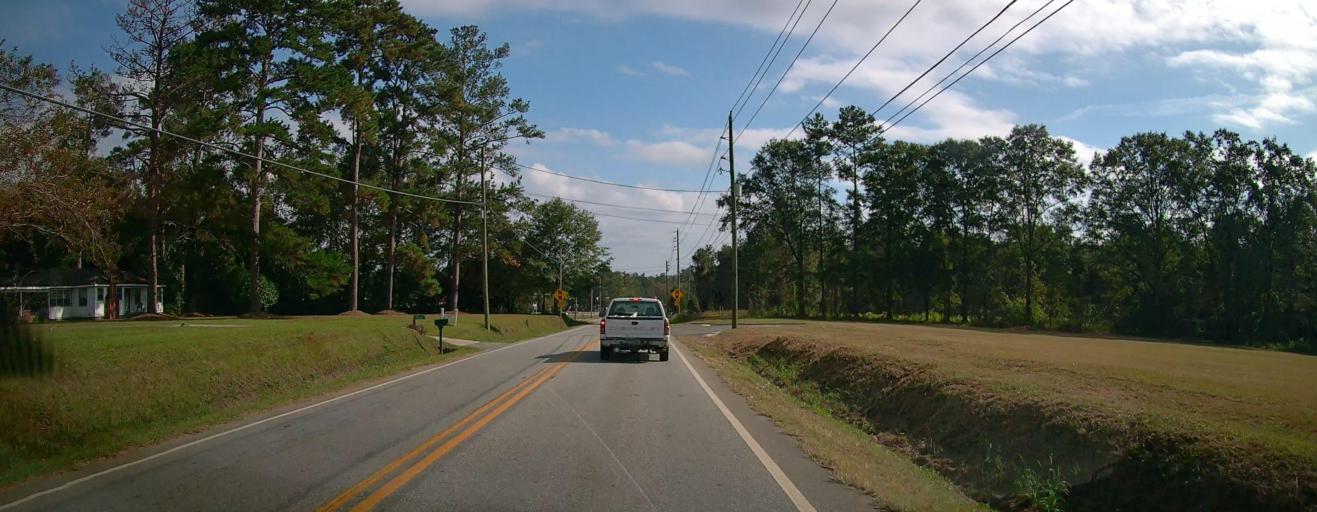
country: US
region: Georgia
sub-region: Thomas County
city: Thomasville
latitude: 30.8711
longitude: -84.0017
